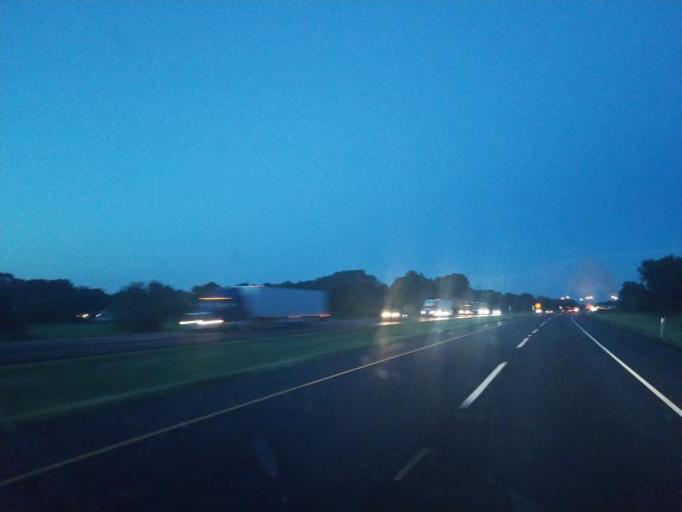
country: US
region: Indiana
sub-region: Elkhart County
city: Simonton Lake
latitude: 41.7331
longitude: -86.0313
